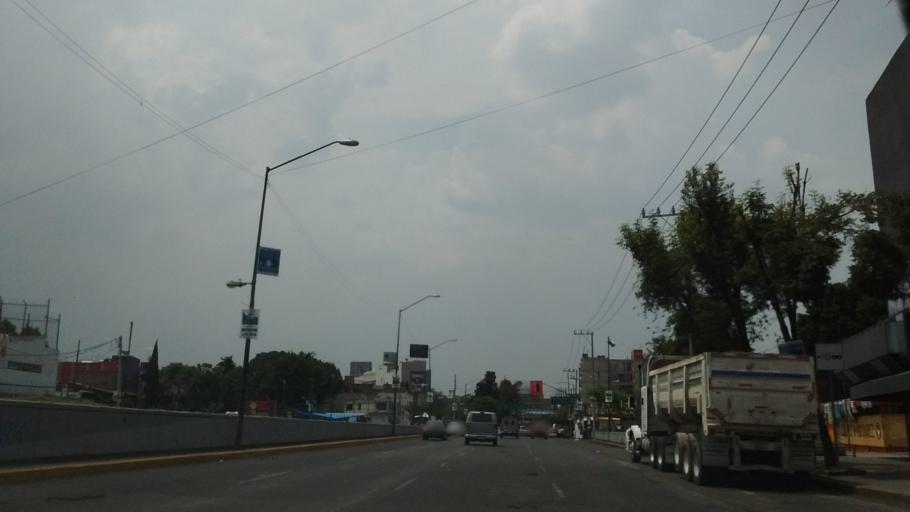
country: MX
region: Mexico City
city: Mexico City
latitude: 19.4058
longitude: -99.1259
